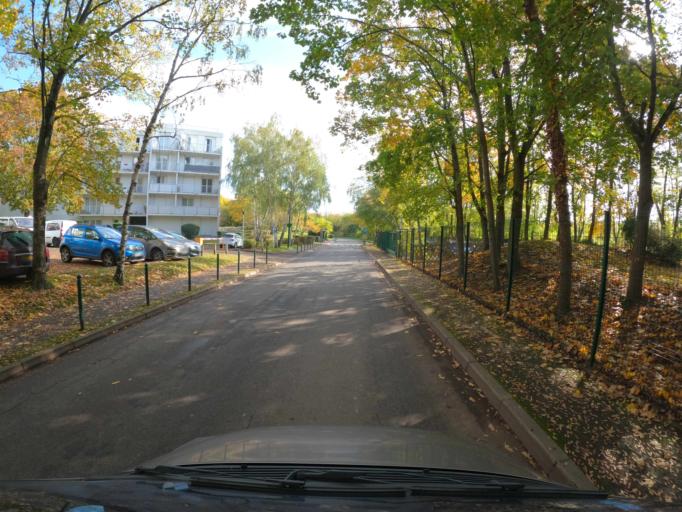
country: FR
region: Ile-de-France
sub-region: Departement de Seine-et-Marne
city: Vaires-sur-Marne
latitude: 48.8763
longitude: 2.6413
